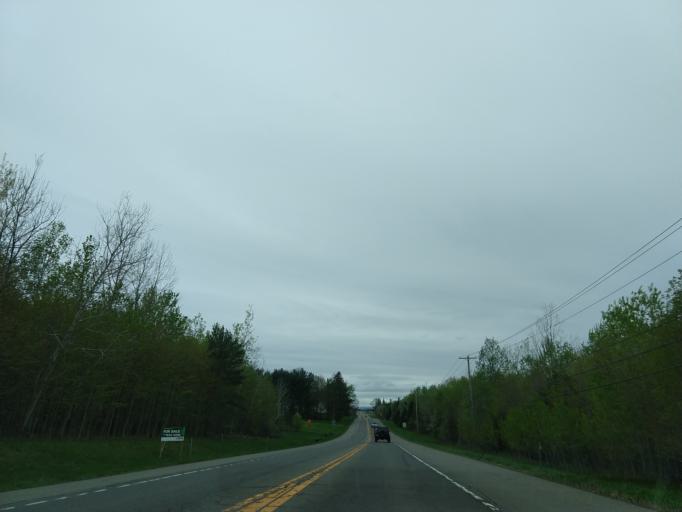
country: US
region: New York
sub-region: Tompkins County
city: Northeast Ithaca
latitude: 42.4747
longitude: -76.3921
